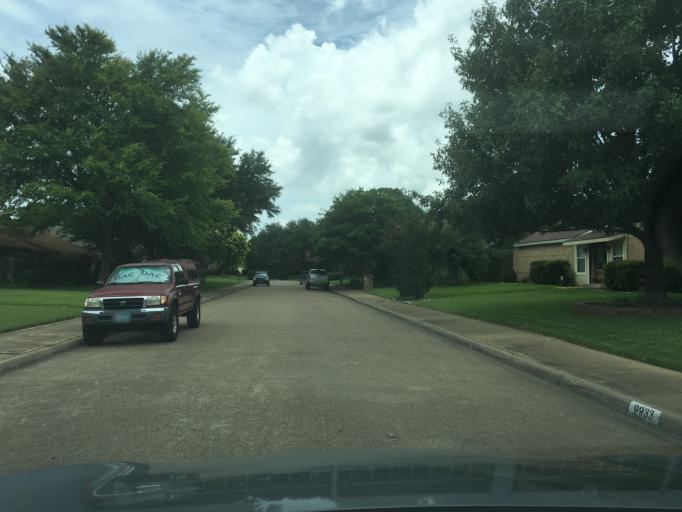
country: US
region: Texas
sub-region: Dallas County
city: Richardson
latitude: 32.9282
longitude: -96.7150
